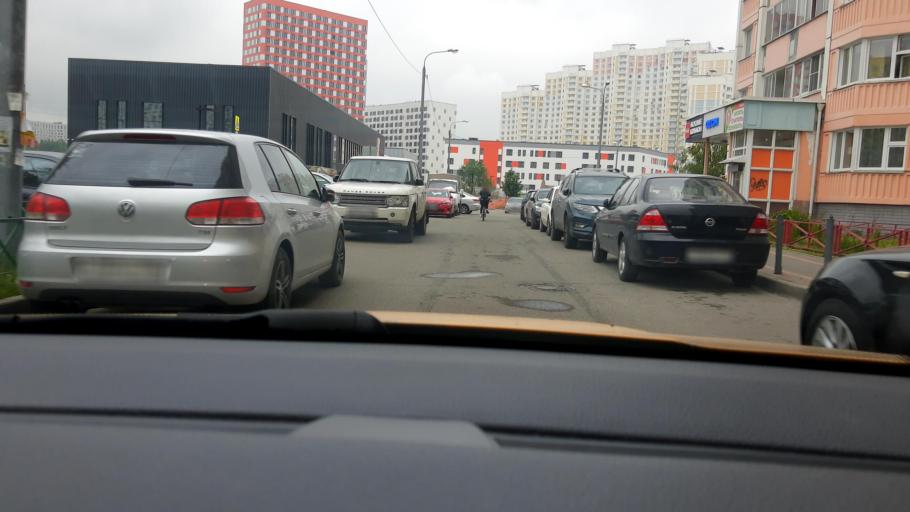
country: RU
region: Moskovskaya
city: Mytishchi
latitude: 55.9164
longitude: 37.7142
